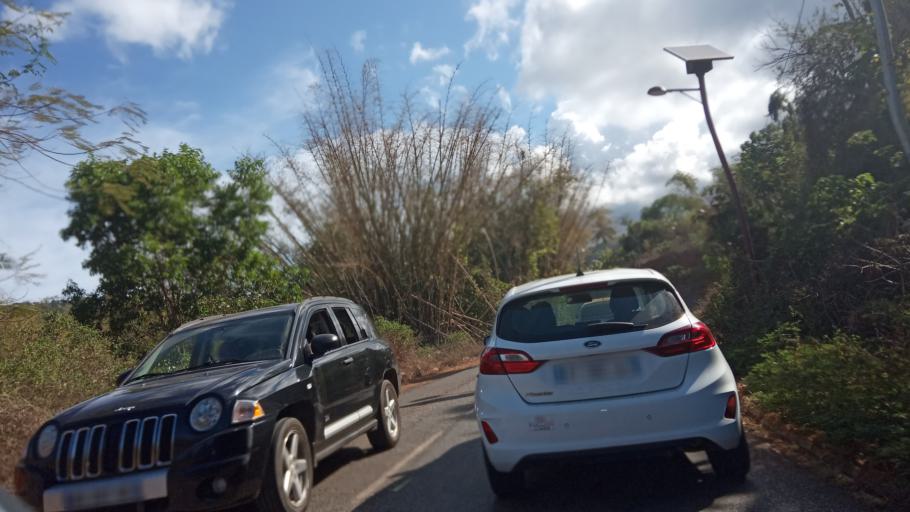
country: YT
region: Dembeni
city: Dembeni
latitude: -12.8682
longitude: 45.1991
